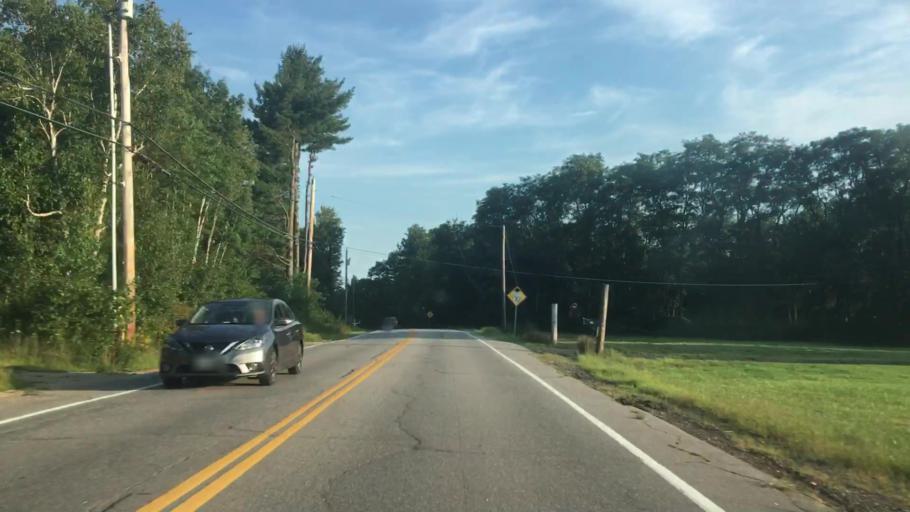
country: US
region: New Hampshire
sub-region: Belknap County
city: Gilmanton
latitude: 43.4364
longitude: -71.4170
